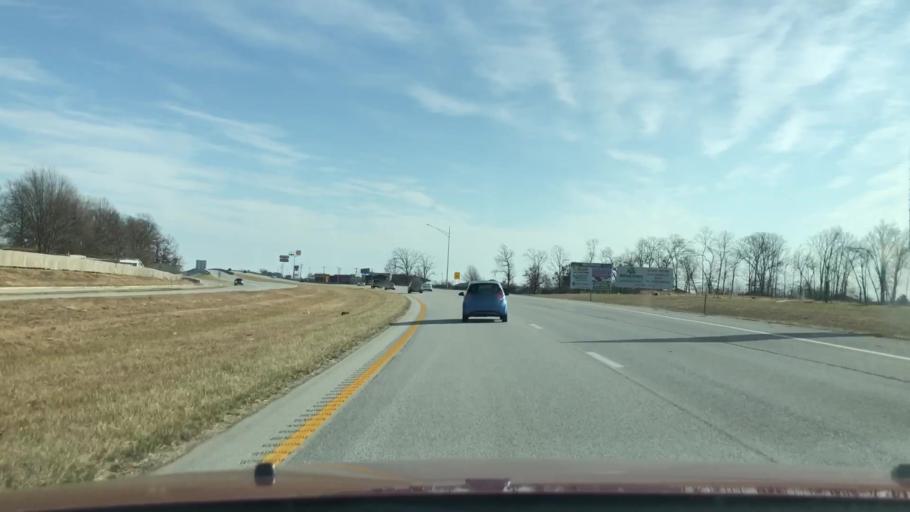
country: US
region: Missouri
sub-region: Webster County
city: Rogersville
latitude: 37.1097
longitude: -93.0644
